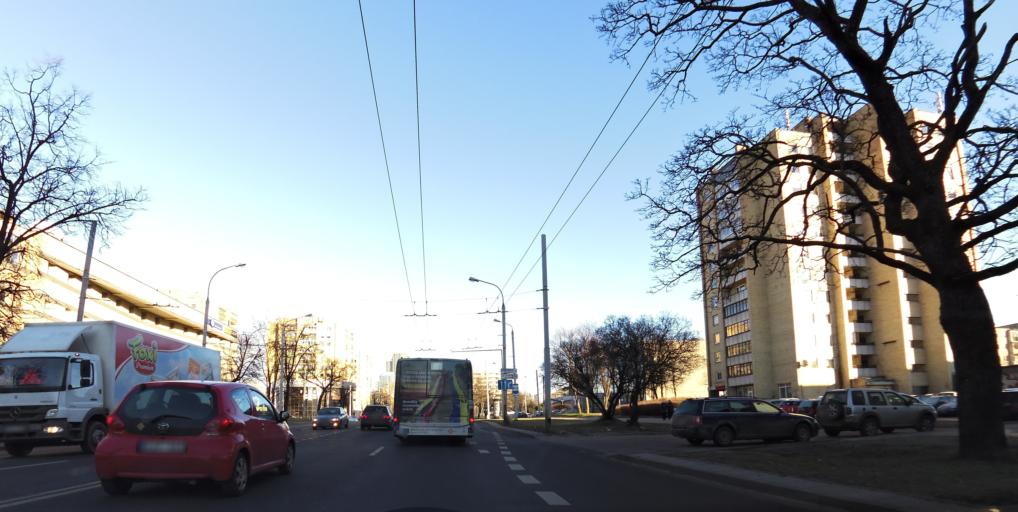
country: LT
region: Vilnius County
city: Vilkpede
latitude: 54.6747
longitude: 25.2498
